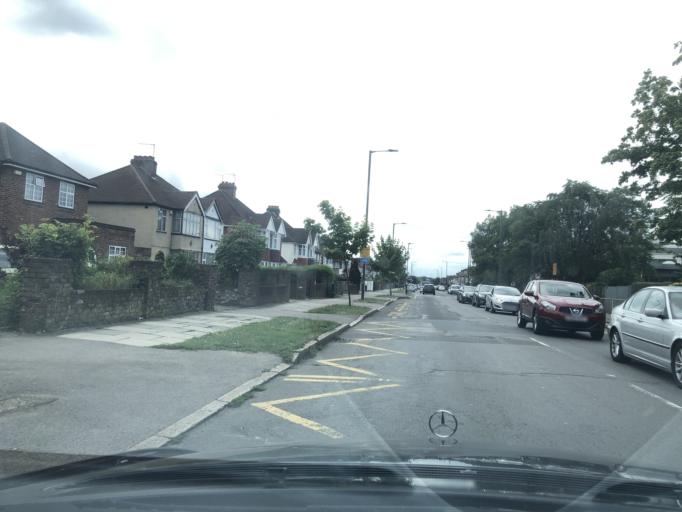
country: GB
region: England
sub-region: Greater London
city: Northolt
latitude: 51.5628
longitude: -0.3692
